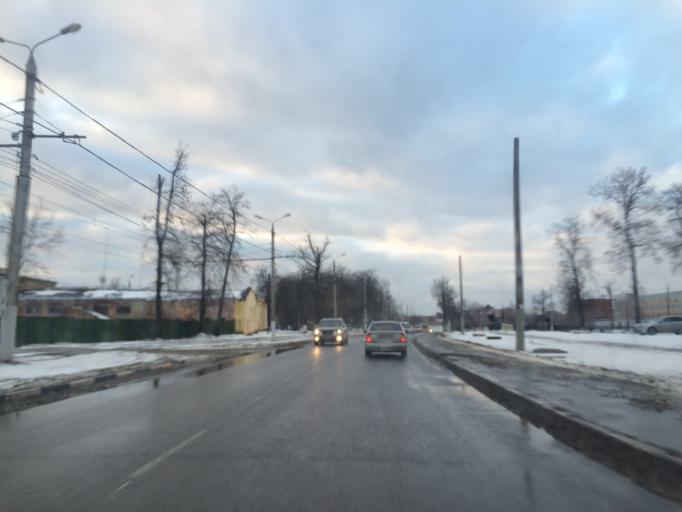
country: RU
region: Tula
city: Tula
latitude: 54.2199
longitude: 37.6957
